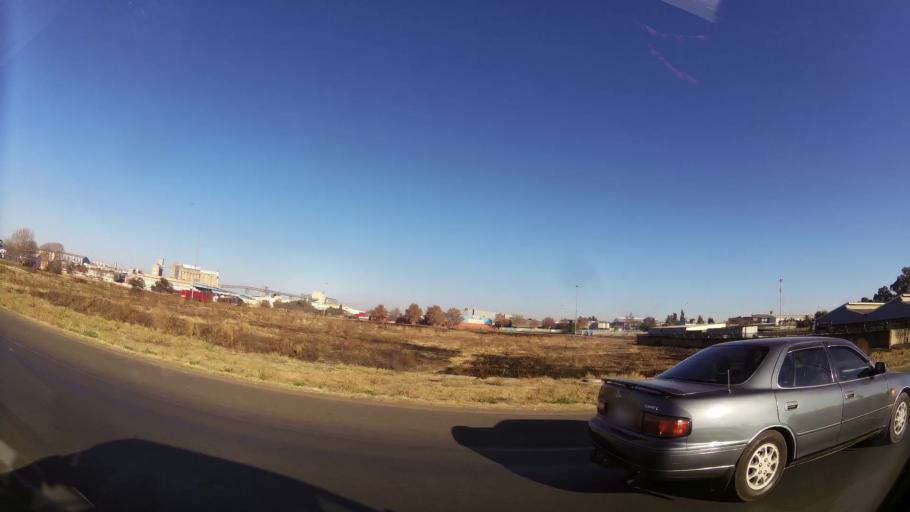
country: ZA
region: Gauteng
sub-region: Ekurhuleni Metropolitan Municipality
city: Germiston
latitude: -26.3063
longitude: 28.1379
